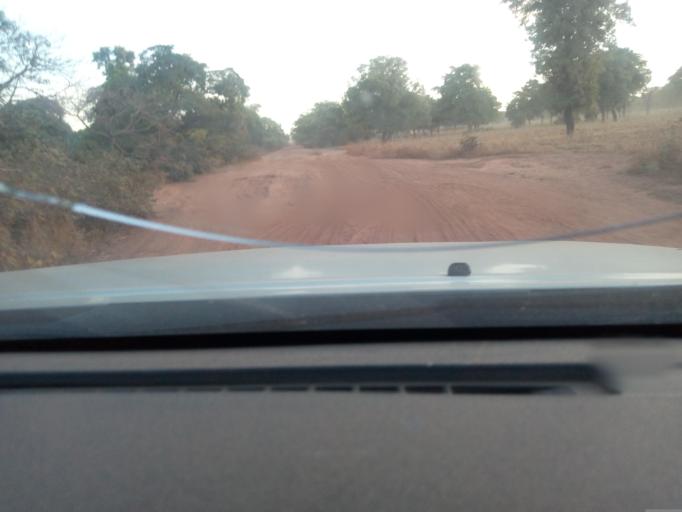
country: ML
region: Koulikoro
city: Dioila
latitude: 12.1855
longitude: -6.1840
